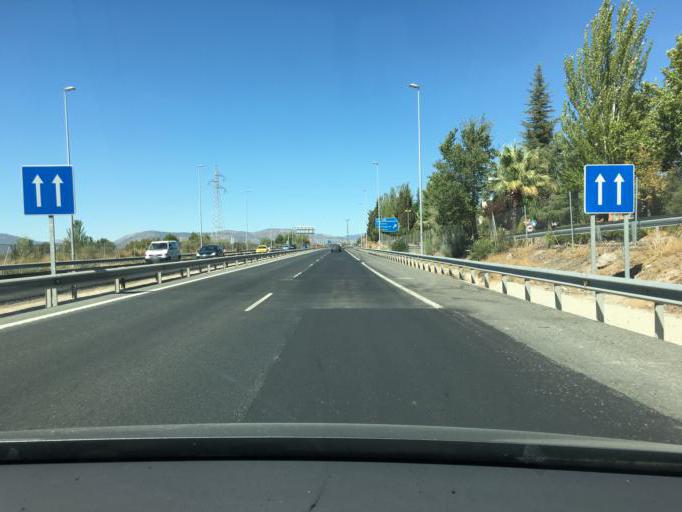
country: ES
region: Andalusia
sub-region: Provincia de Granada
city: Albolote
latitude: 37.2498
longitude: -3.6564
